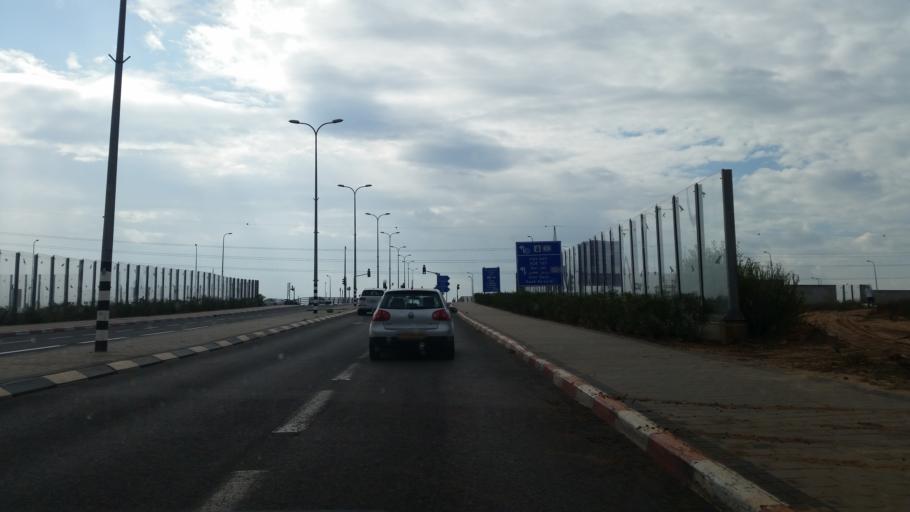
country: IL
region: Central District
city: Ra'anana
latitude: 32.1735
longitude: 34.8686
